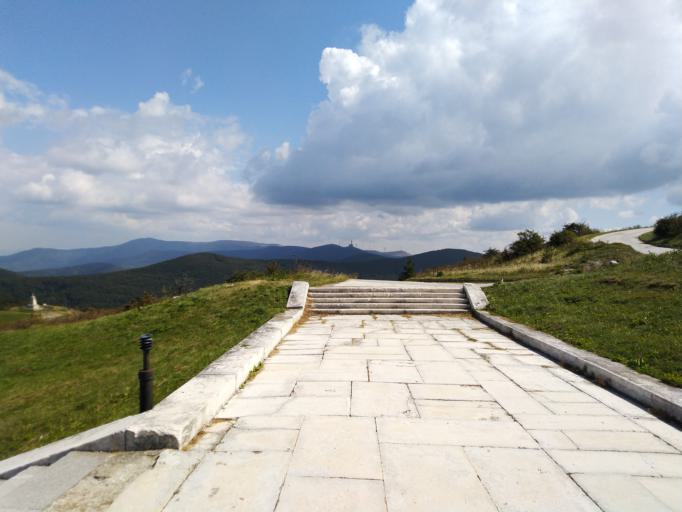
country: BG
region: Stara Zagora
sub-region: Obshtina Kazanluk
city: Shipka
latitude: 42.7487
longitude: 25.3218
